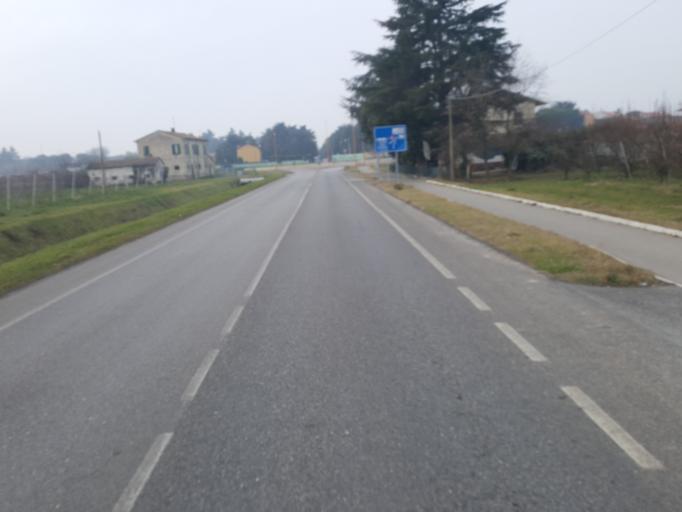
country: IT
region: Emilia-Romagna
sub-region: Forli-Cesena
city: Cesena
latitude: 44.1557
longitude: 12.2723
